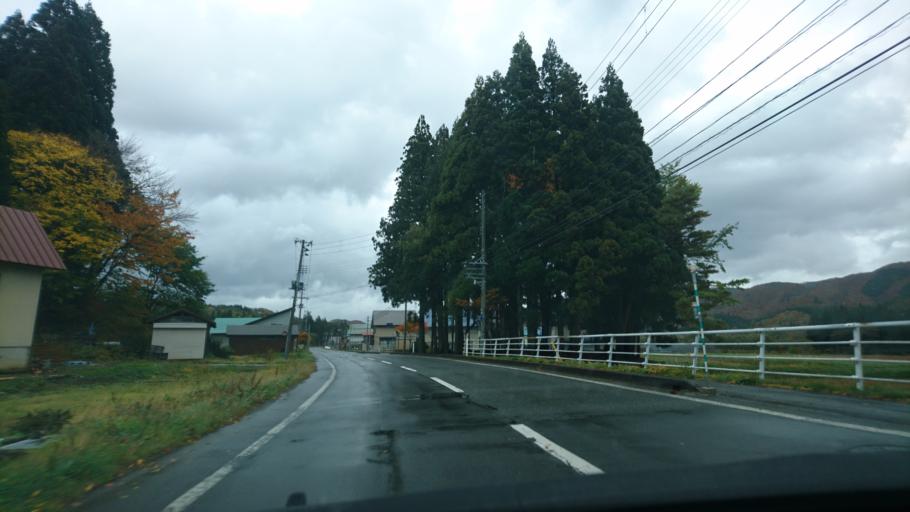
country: JP
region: Akita
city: Kakunodatemachi
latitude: 39.4910
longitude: 140.8111
